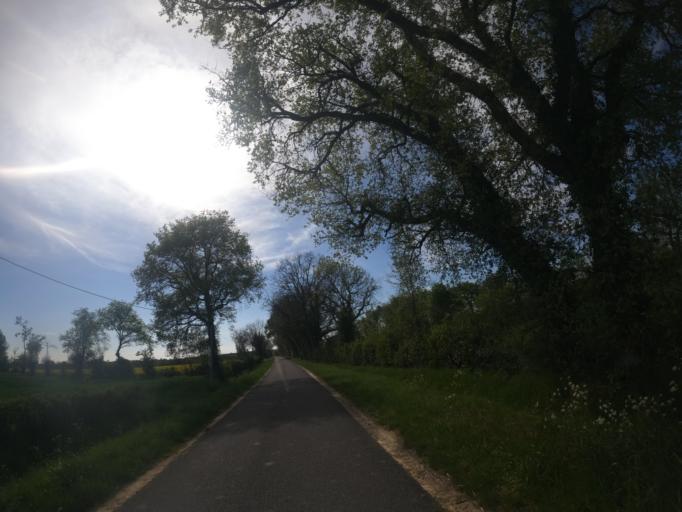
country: FR
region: Poitou-Charentes
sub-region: Departement des Deux-Sevres
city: Saint-Varent
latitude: 46.9171
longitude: -0.2475
